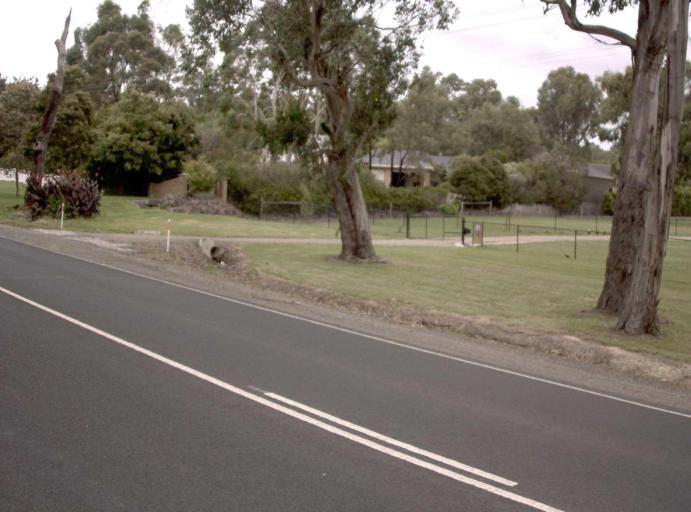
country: AU
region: Victoria
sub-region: Yarra Ranges
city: Mount Evelyn
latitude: -37.7537
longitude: 145.3799
